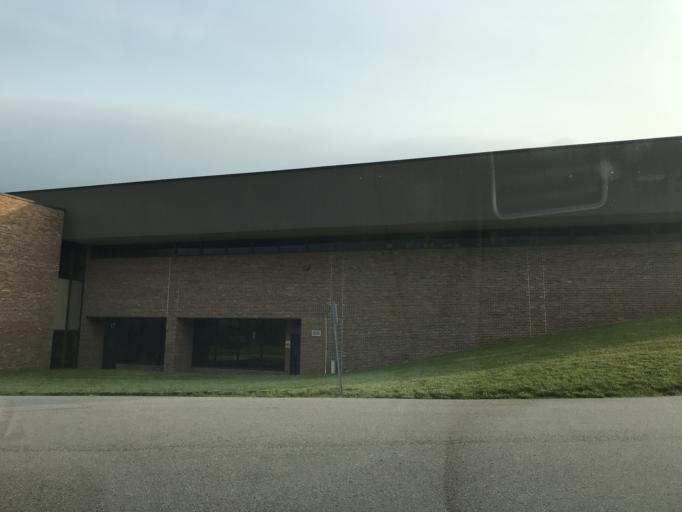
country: US
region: Michigan
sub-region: Livingston County
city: Brighton
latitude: 42.5251
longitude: -83.7941
